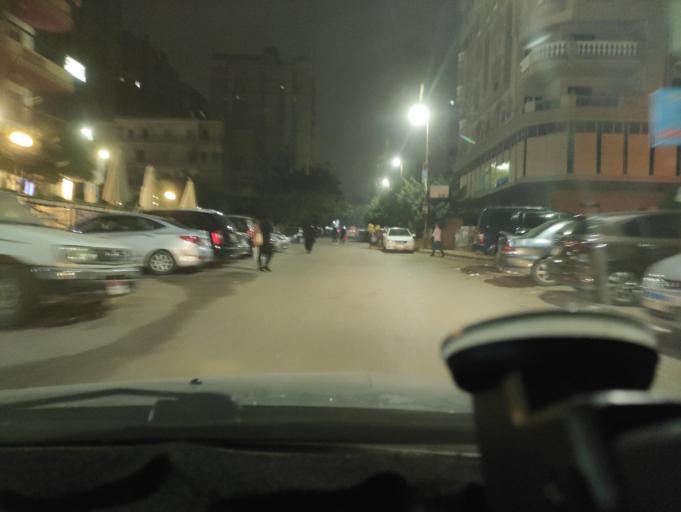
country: EG
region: Muhafazat al Qahirah
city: Cairo
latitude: 30.0590
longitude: 31.3366
